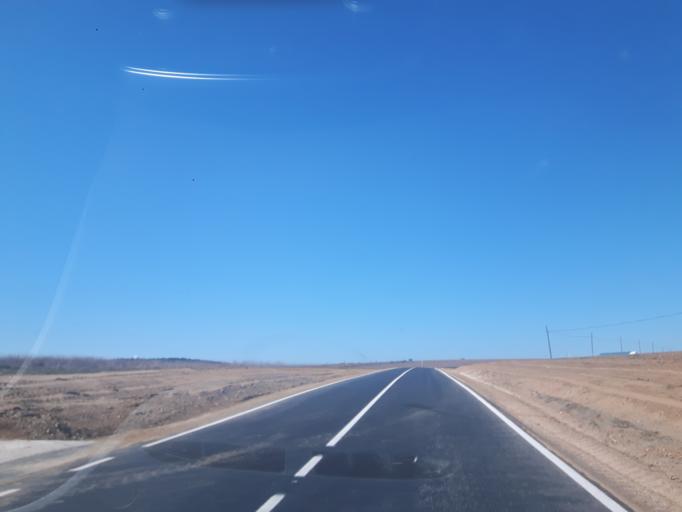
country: ES
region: Castille and Leon
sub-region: Provincia de Salamanca
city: Terradillos
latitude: 40.8230
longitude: -5.5315
